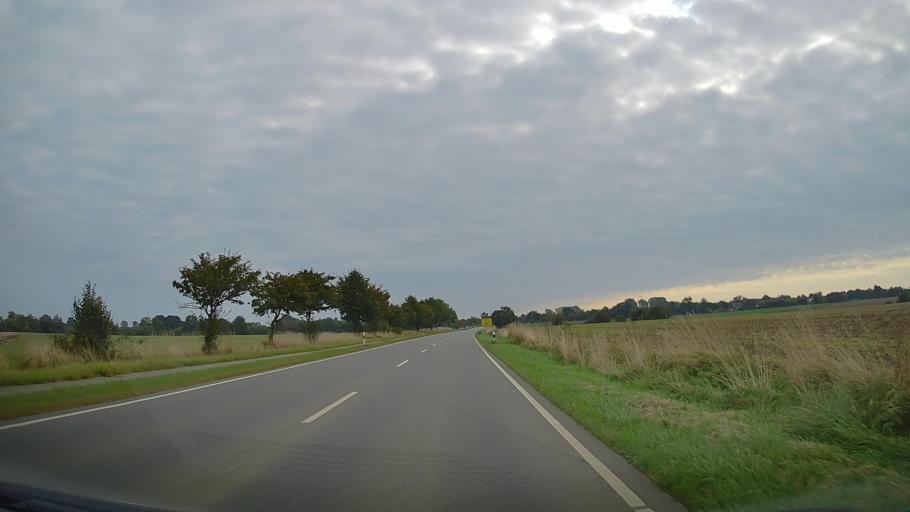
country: DE
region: Schleswig-Holstein
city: Krummbek
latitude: 54.3973
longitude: 10.4160
